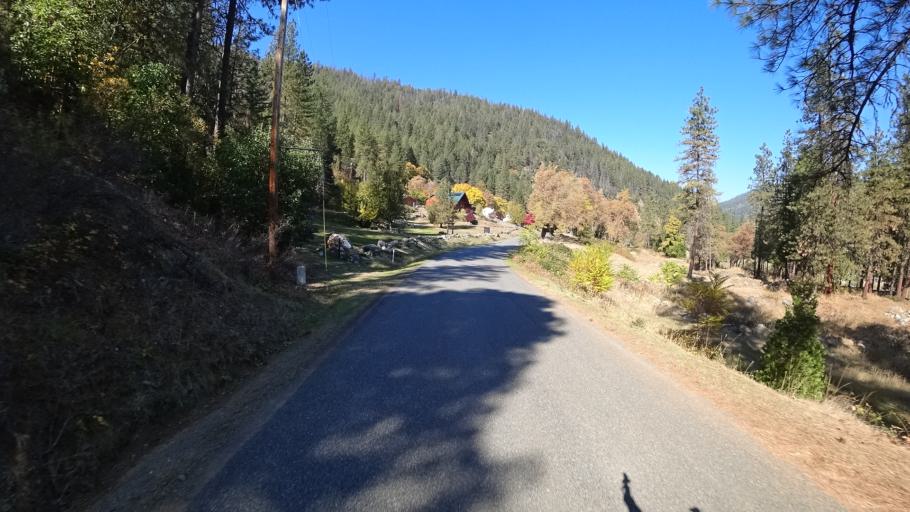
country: US
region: California
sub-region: Siskiyou County
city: Yreka
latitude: 41.7465
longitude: -123.0079
